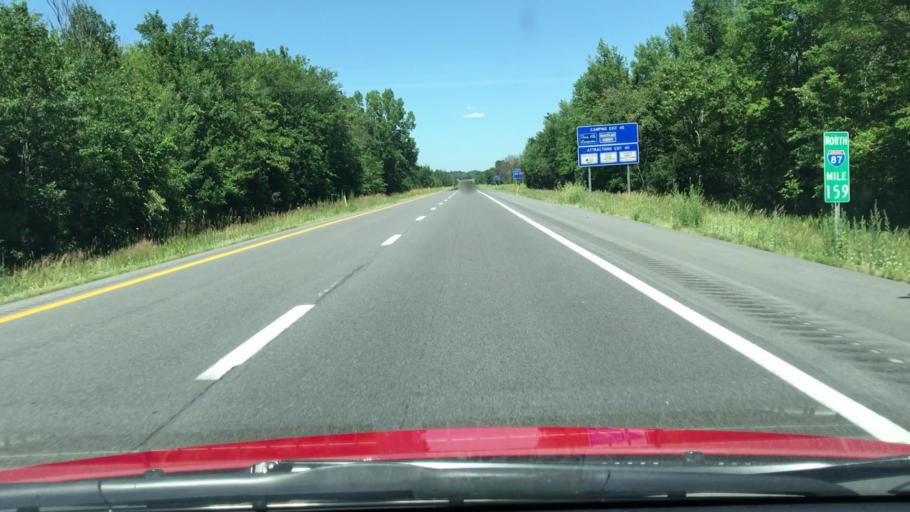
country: US
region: New York
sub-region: Clinton County
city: Cumberland Head
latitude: 44.7670
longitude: -73.4324
